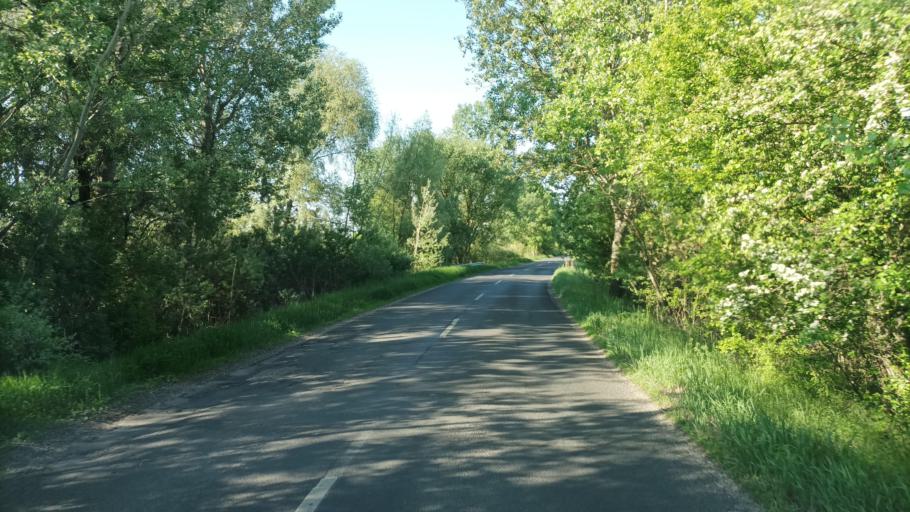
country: HU
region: Pest
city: Monor
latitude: 47.3073
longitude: 19.4398
